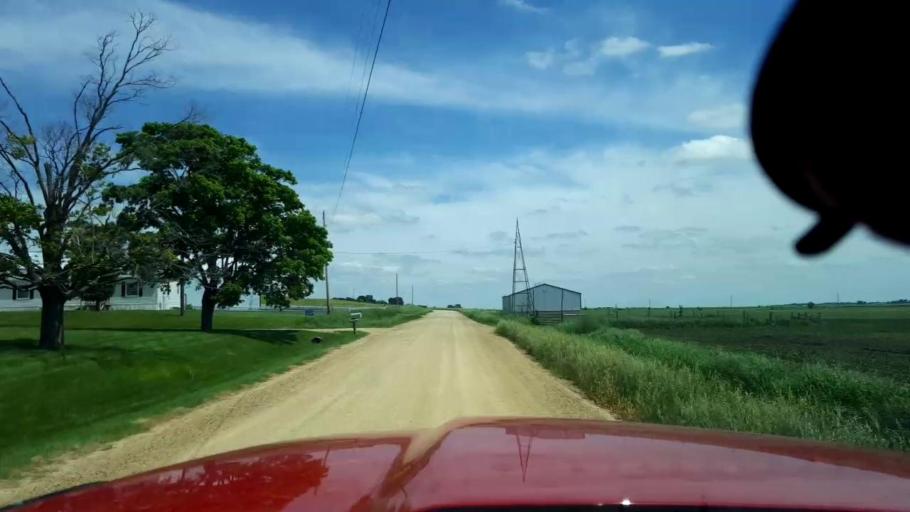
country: US
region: Iowa
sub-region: Linn County
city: Lisbon
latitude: 41.9522
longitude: -91.3554
